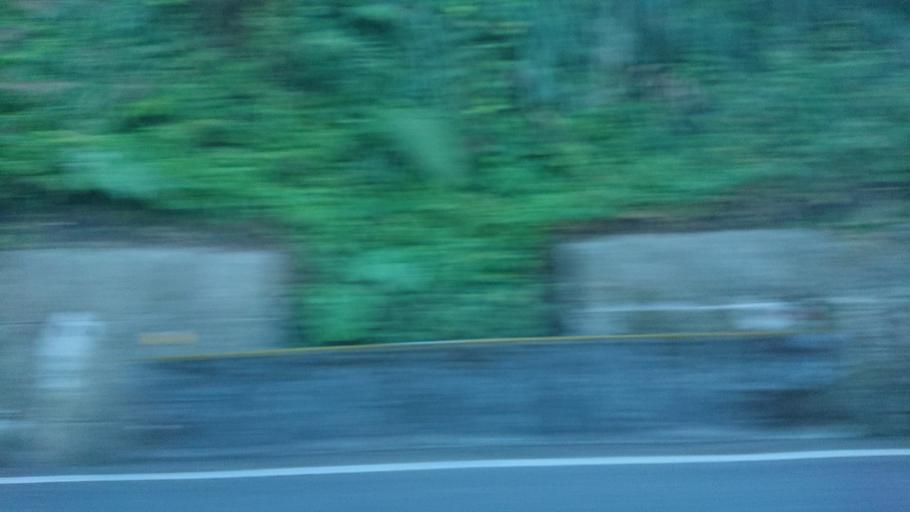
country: TW
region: Taiwan
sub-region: Chiayi
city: Jiayi Shi
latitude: 23.4626
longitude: 120.7225
